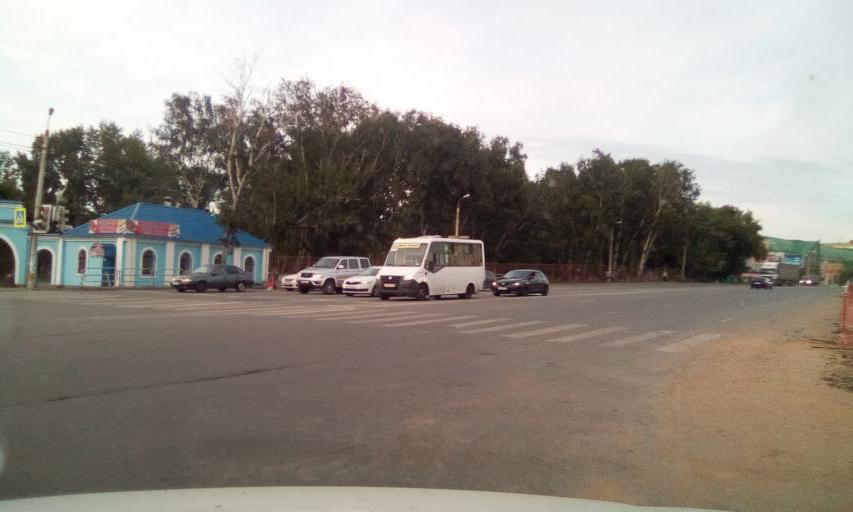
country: RU
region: Chelyabinsk
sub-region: Gorod Chelyabinsk
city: Chelyabinsk
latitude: 55.1668
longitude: 61.4531
